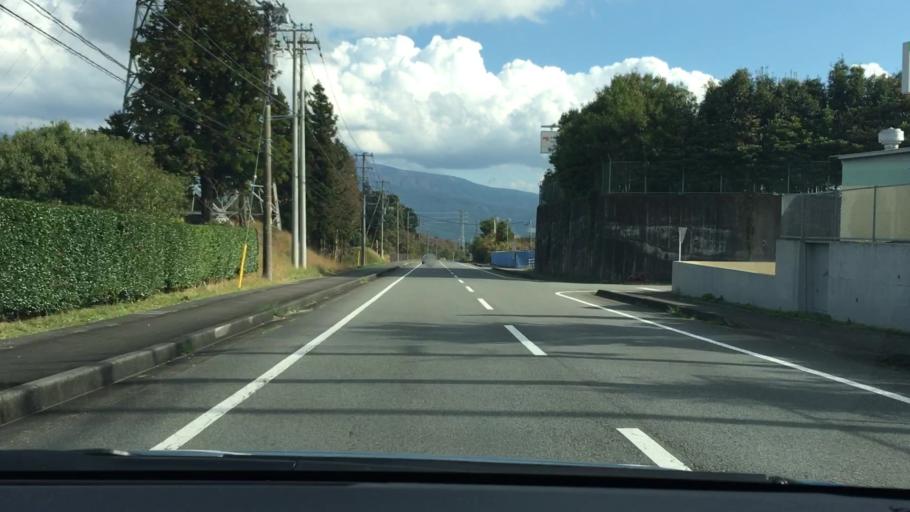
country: JP
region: Shizuoka
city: Gotemba
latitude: 35.2269
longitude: 138.8890
